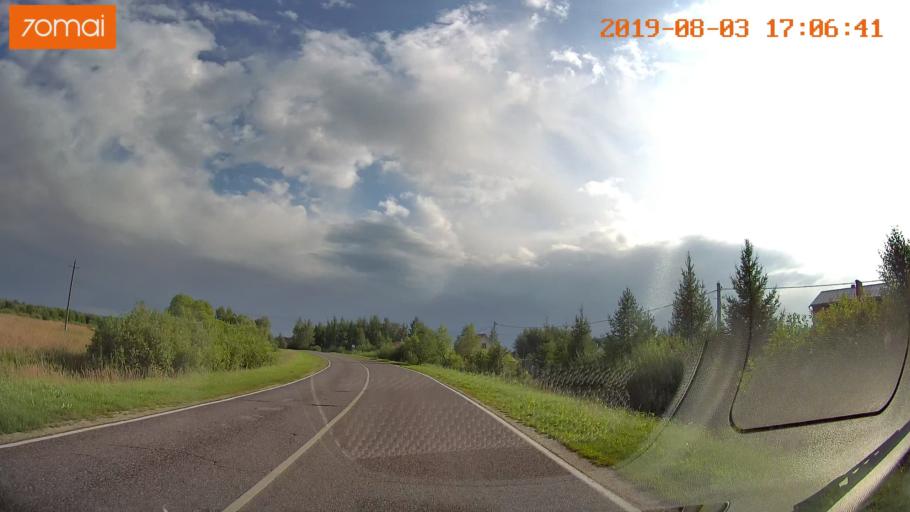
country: RU
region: Moskovskaya
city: Troitskoye
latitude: 55.3052
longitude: 38.5490
